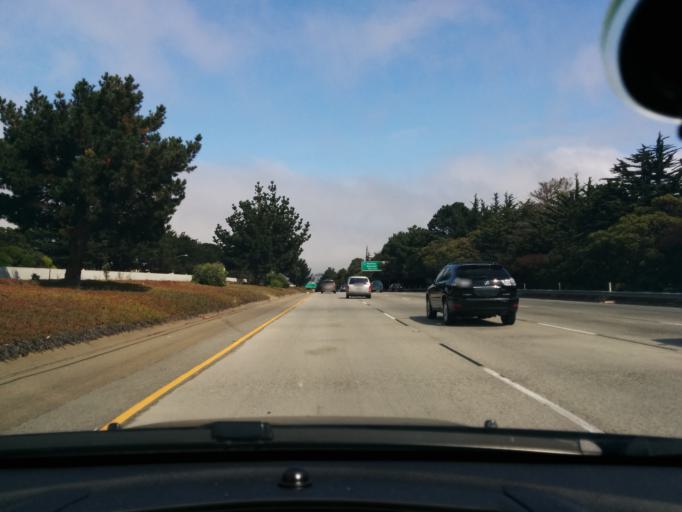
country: US
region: California
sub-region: San Mateo County
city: Colma
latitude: 37.6646
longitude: -122.4656
